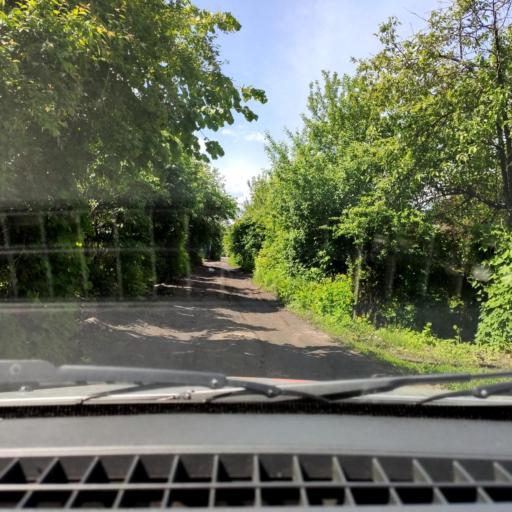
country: RU
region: Voronezj
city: Voronezh
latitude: 51.5929
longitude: 39.1604
